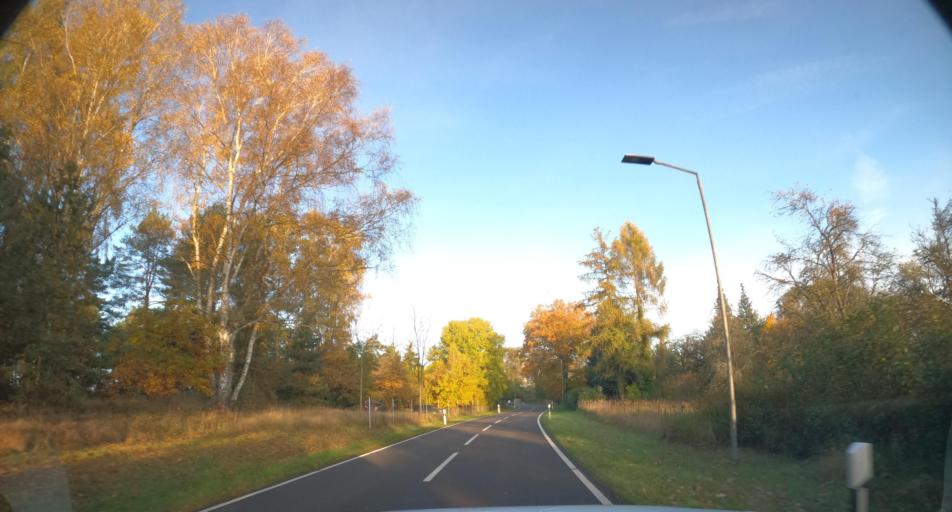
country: DE
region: Mecklenburg-Vorpommern
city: Ahlbeck
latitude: 53.6426
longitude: 14.2040
